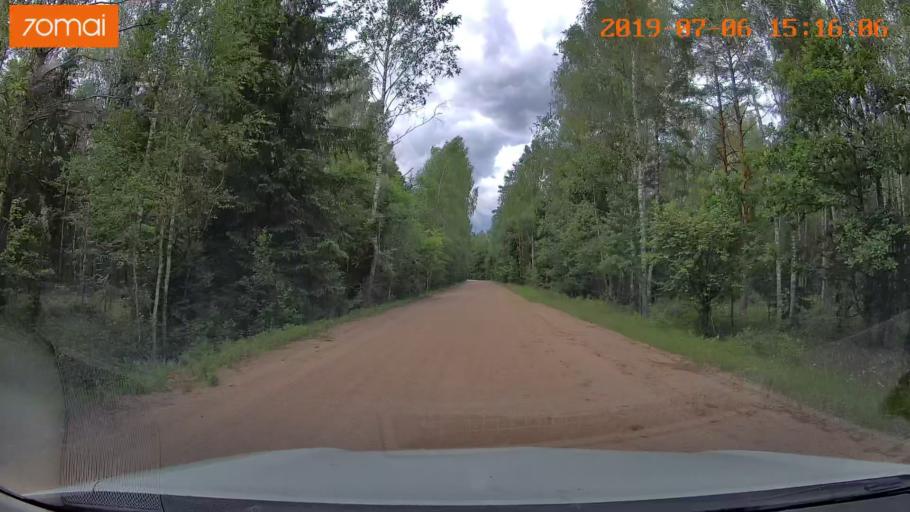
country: BY
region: Minsk
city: Ivyanyets
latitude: 53.9784
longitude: 26.6808
